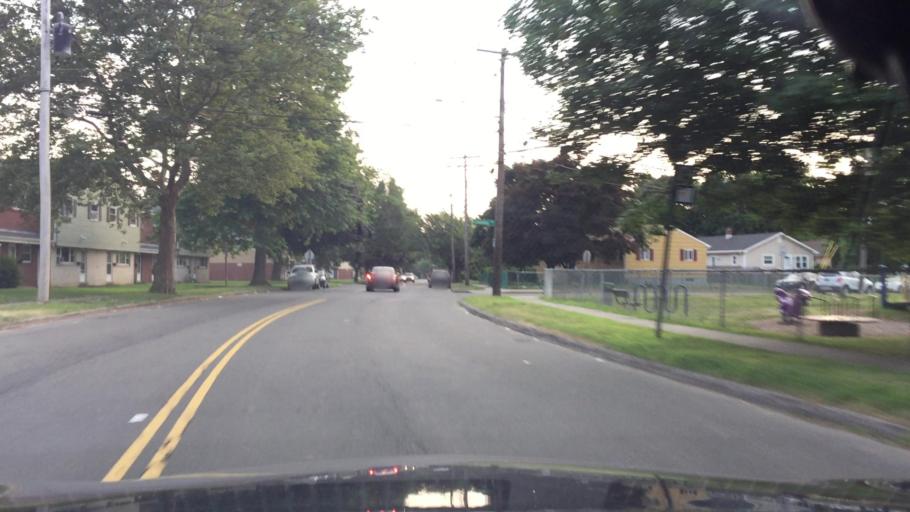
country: US
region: Connecticut
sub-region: Fairfield County
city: Stratford
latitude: 41.1749
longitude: -73.1332
